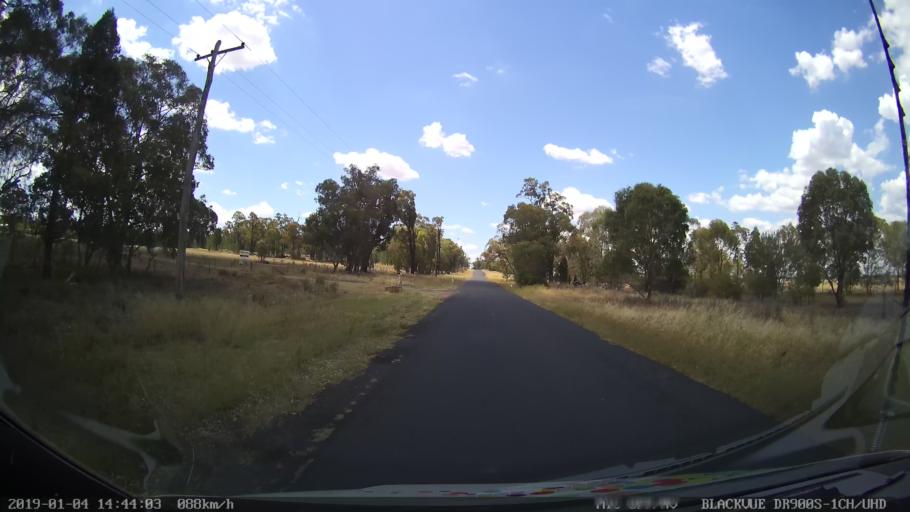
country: AU
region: New South Wales
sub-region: Dubbo Municipality
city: Dubbo
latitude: -32.1112
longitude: 148.6548
